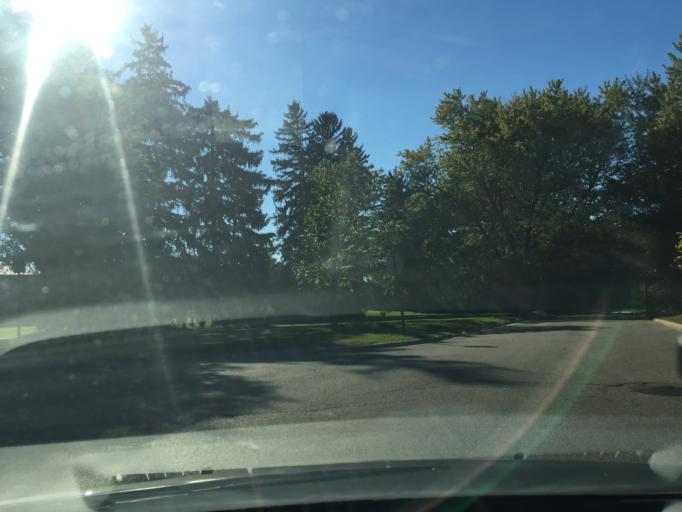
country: US
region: Michigan
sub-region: Oakland County
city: Bloomfield Hills
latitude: 42.5696
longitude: -83.2516
